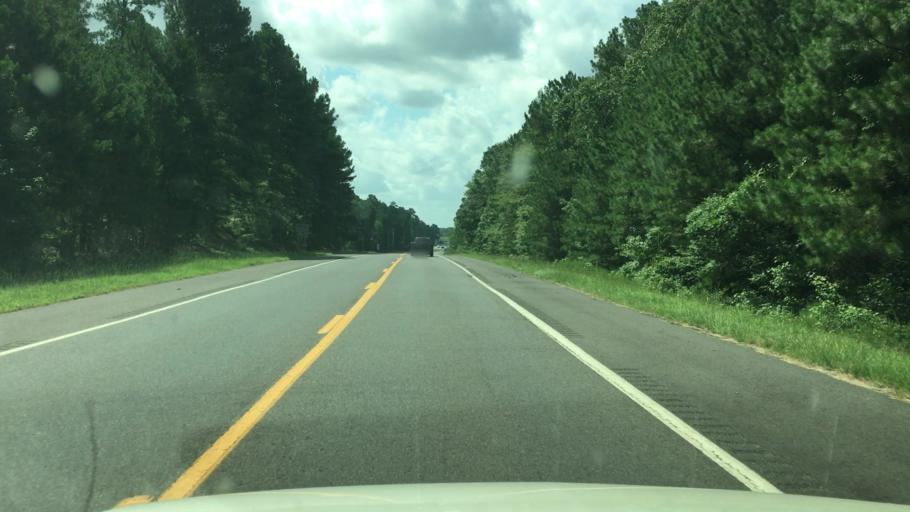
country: US
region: Arkansas
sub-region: Clark County
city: Arkadelphia
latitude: 34.1972
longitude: -93.0762
